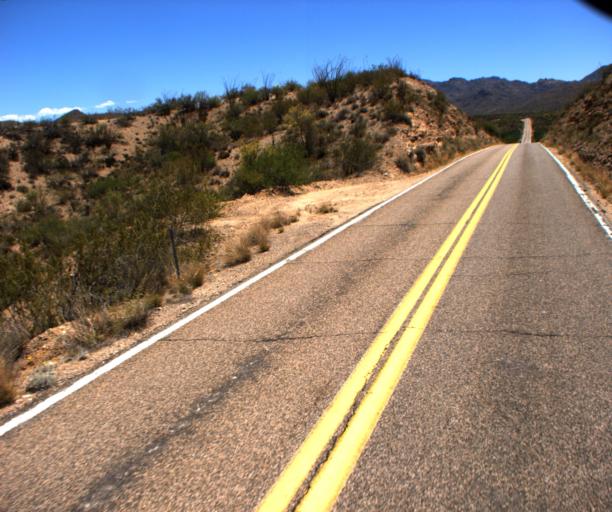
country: US
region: Arizona
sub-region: Yavapai County
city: Bagdad
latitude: 34.4835
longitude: -113.0634
